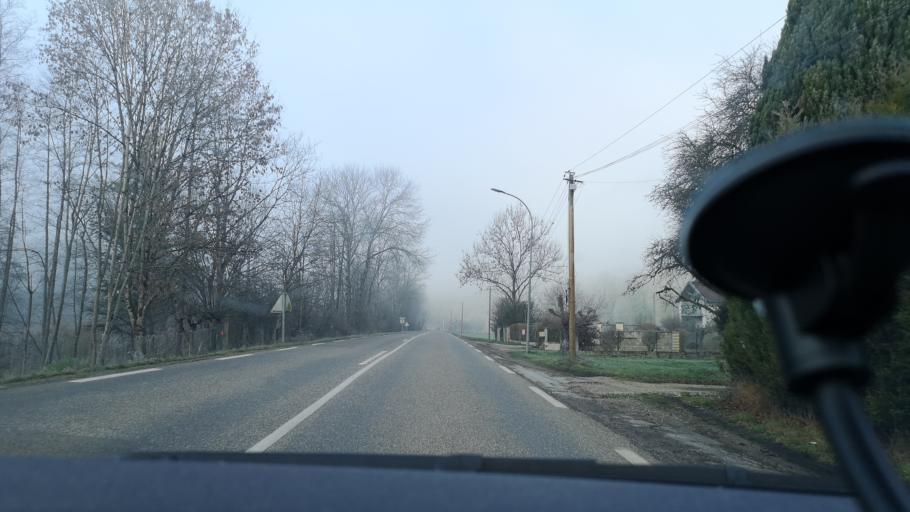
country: FR
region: Franche-Comte
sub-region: Departement du Doubs
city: Clerval
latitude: 47.3642
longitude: 6.4461
